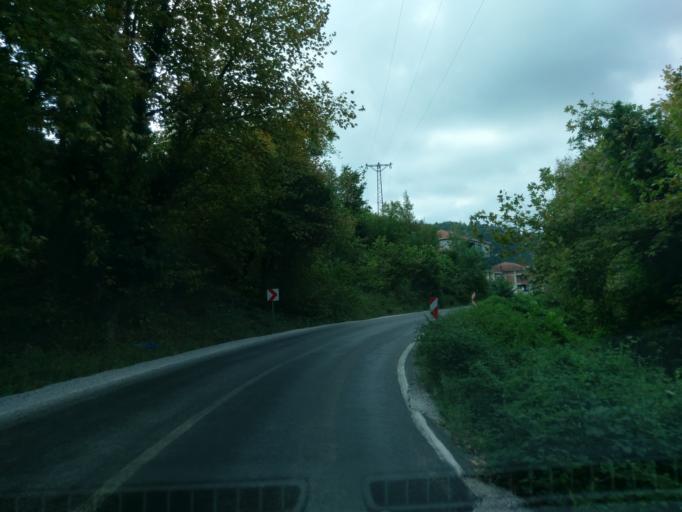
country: TR
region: Sinop
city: Helaldi
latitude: 41.9289
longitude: 34.4164
